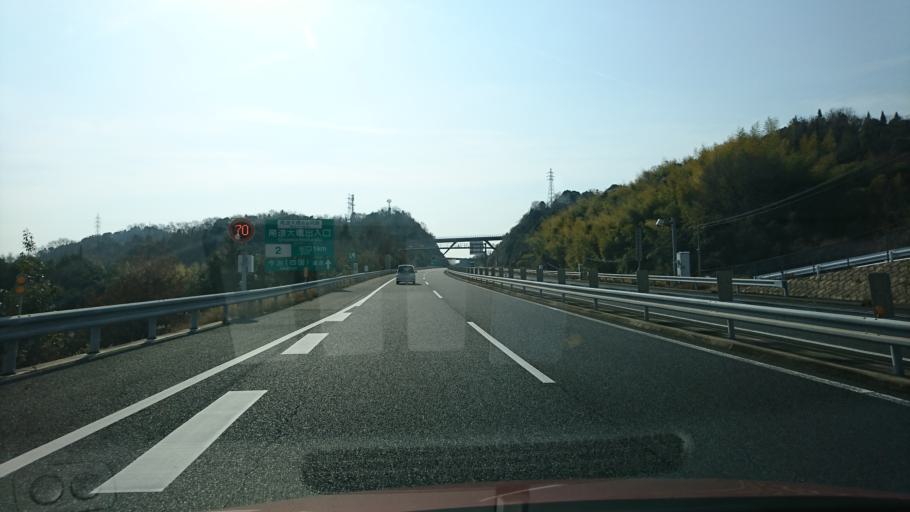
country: JP
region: Hiroshima
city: Onomichi
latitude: 34.4264
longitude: 133.2193
